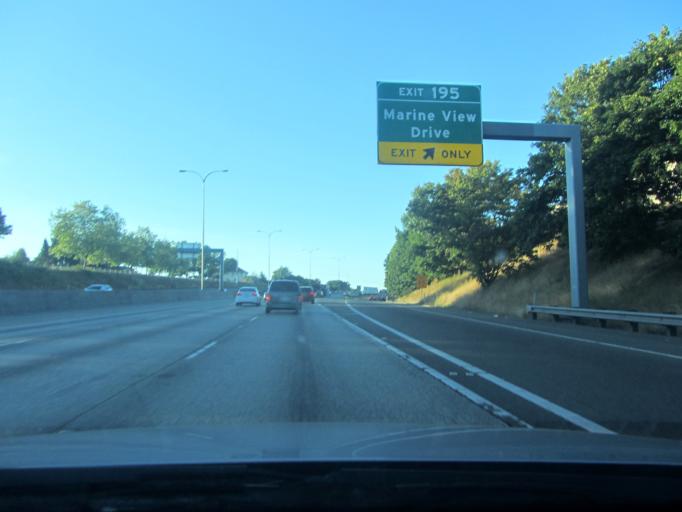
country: US
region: Washington
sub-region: Snohomish County
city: Everett
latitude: 47.9884
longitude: -122.1828
